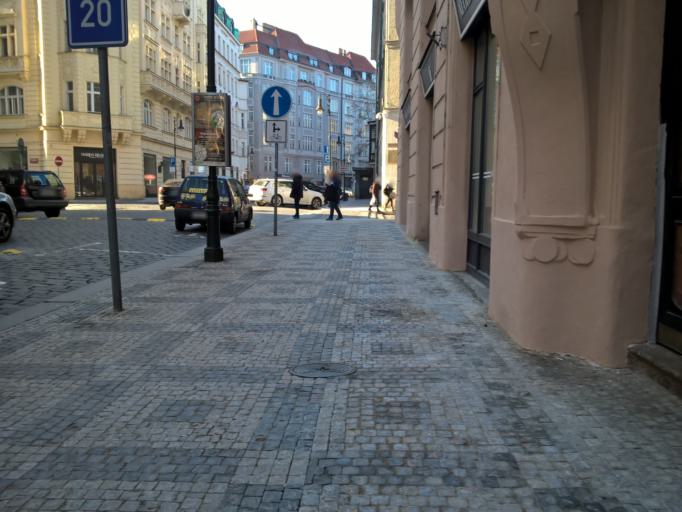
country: CZ
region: Praha
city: Prague
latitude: 50.0894
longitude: 14.4187
